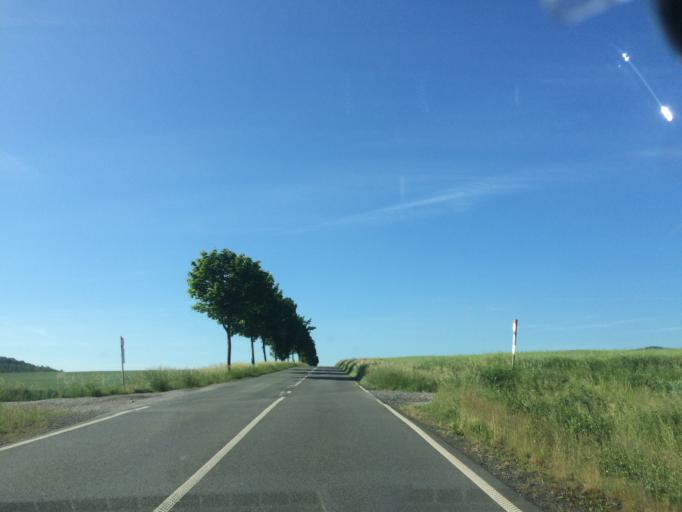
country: DE
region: Hesse
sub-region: Regierungsbezirk Kassel
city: Calden
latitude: 51.3612
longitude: 9.4169
